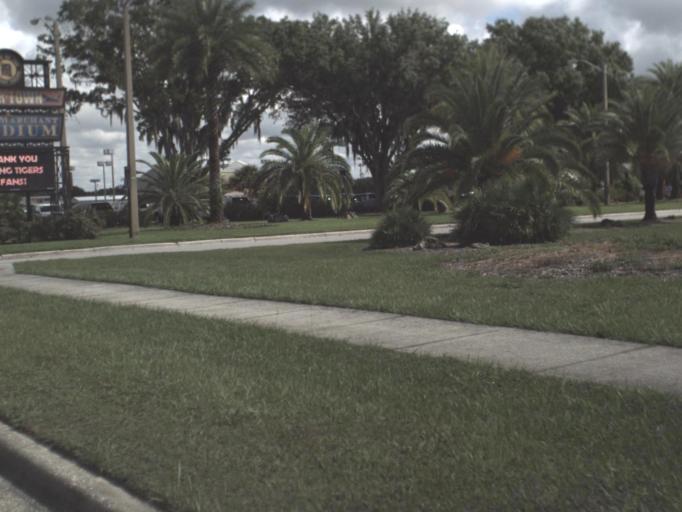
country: US
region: Florida
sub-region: Polk County
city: Lakeland
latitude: 28.0735
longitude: -81.9532
